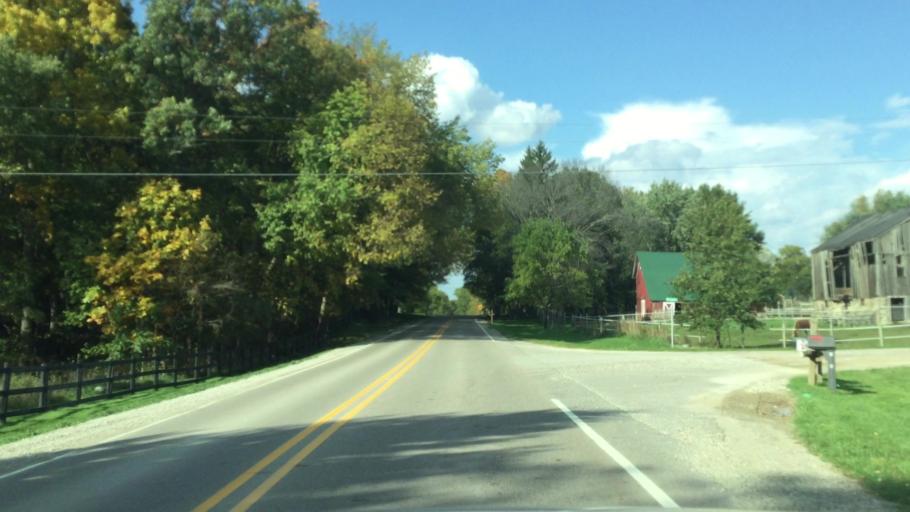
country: US
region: Michigan
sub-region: Oakland County
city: Milford
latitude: 42.6564
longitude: -83.7008
